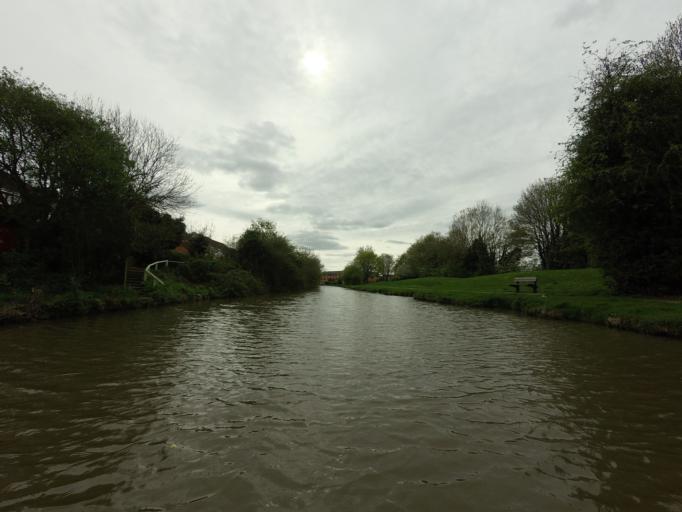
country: GB
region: England
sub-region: Milton Keynes
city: Bradwell
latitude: 52.0640
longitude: -0.7887
